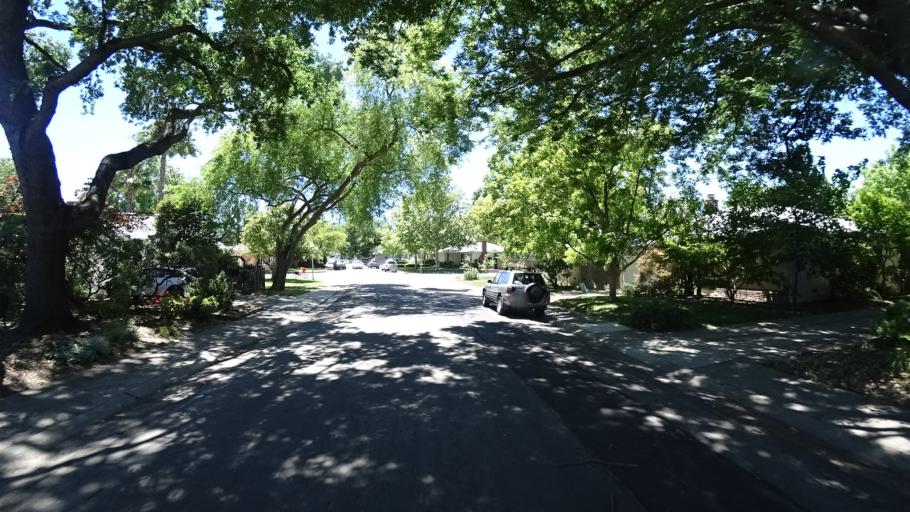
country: US
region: California
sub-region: Sacramento County
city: Sacramento
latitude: 38.5776
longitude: -121.4395
